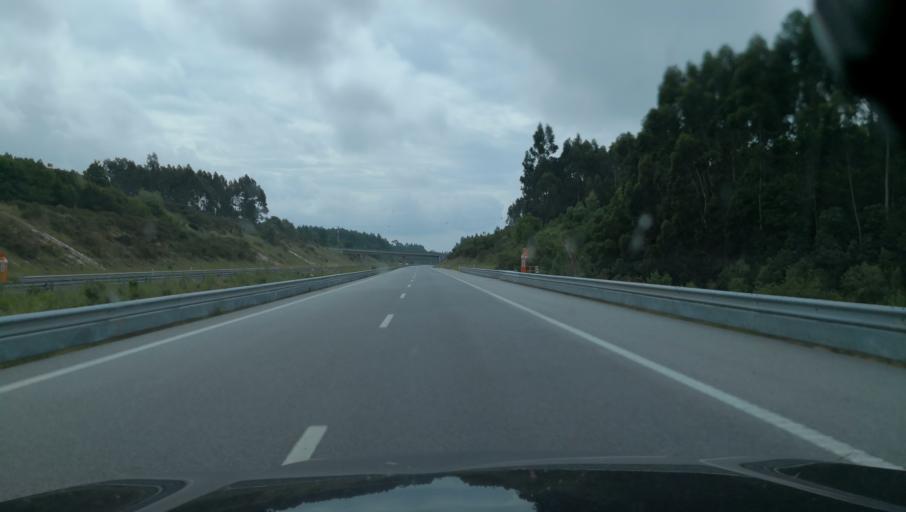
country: PT
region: Coimbra
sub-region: Figueira da Foz
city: Alhadas
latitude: 40.1750
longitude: -8.7972
